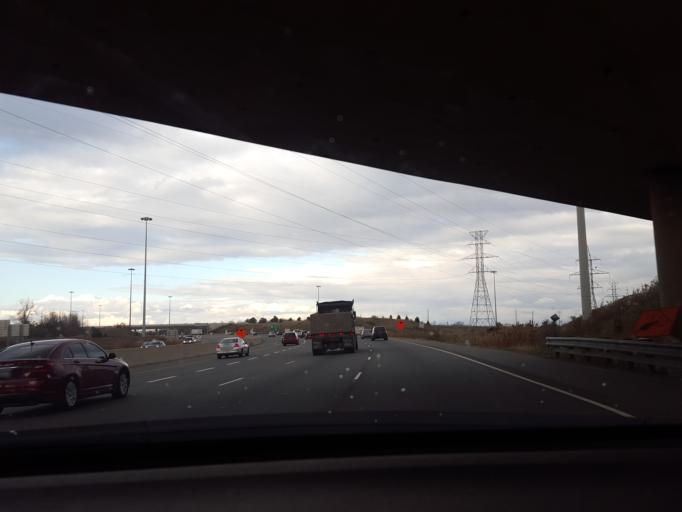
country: CA
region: Ontario
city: Mississauga
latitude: 43.6133
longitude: -79.6318
